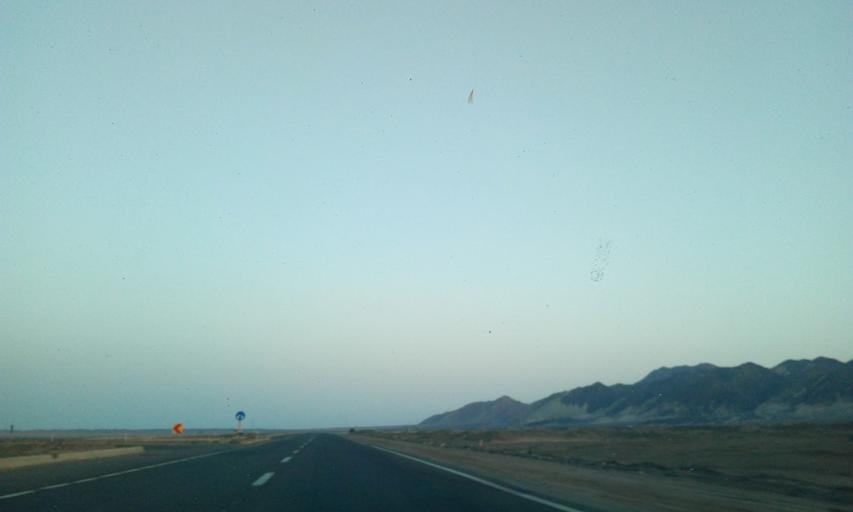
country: EG
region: Red Sea
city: El Gouna
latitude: 27.5401
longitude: 33.5463
